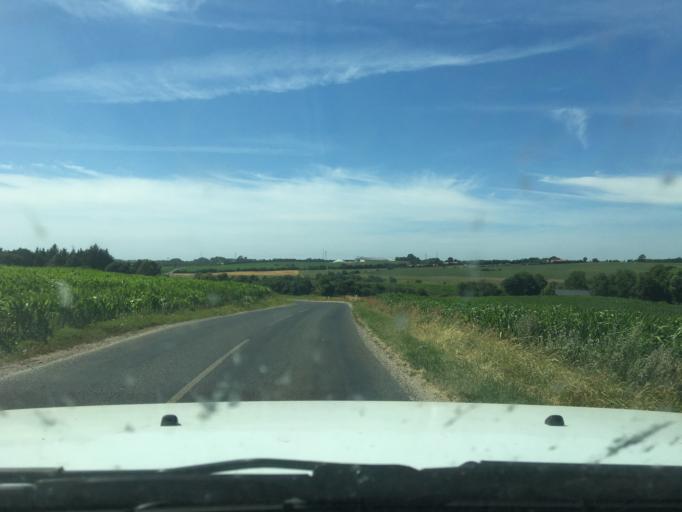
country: DK
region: Central Jutland
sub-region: Viborg Kommune
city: Bjerringbro
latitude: 56.5123
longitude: 9.5922
